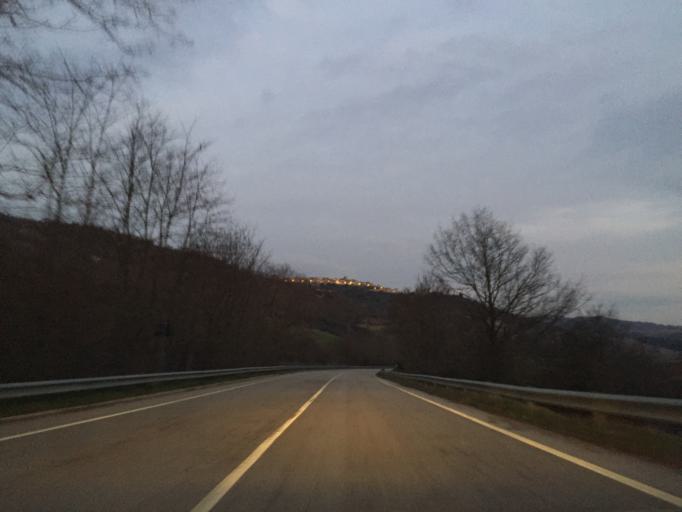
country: IT
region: Apulia
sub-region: Provincia di Foggia
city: Volturara Appula
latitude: 41.4979
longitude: 15.0353
